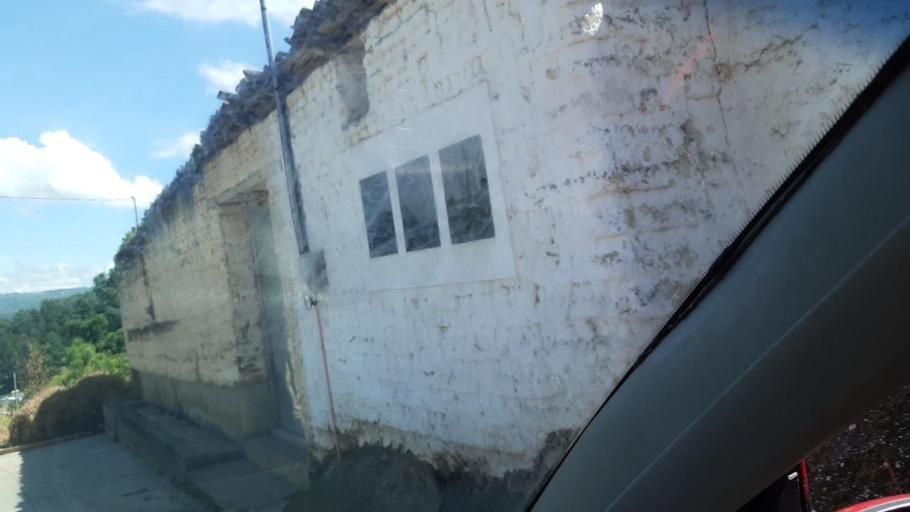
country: GT
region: Quetzaltenango
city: Salcaja
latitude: 14.8669
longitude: -91.4568
